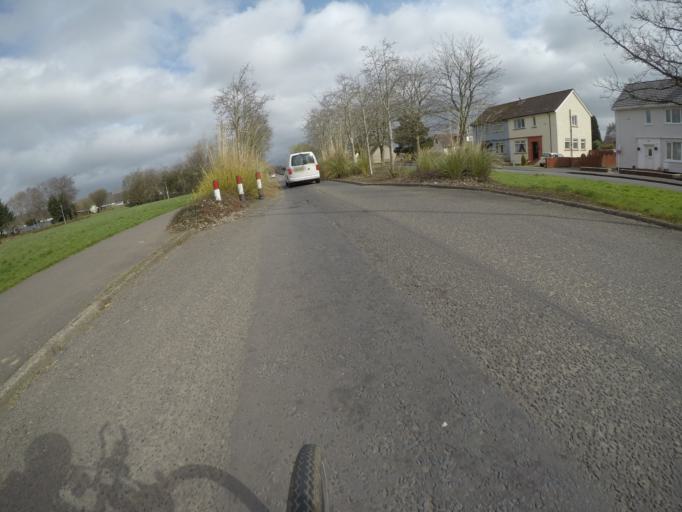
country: GB
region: Scotland
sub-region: North Ayrshire
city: Irvine
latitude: 55.6264
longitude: -4.6408
